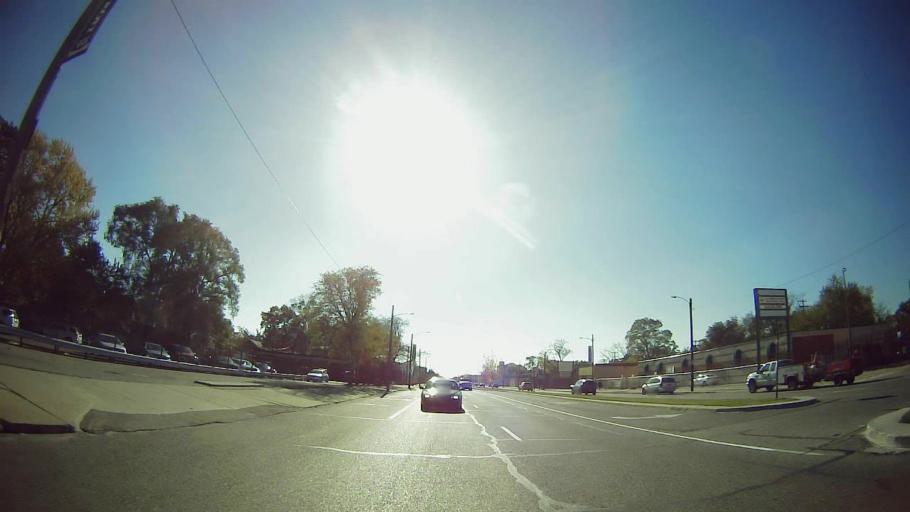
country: US
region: Michigan
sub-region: Oakland County
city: Ferndale
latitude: 42.4448
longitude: -83.1418
